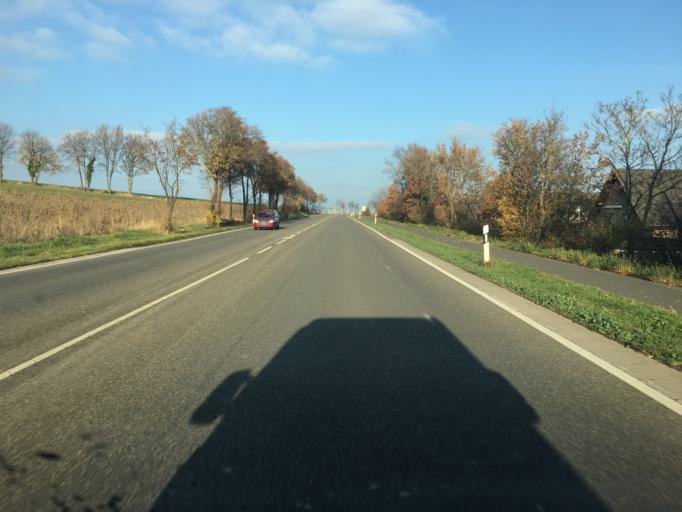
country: DE
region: North Rhine-Westphalia
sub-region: Regierungsbezirk Koln
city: Mechernich
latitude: 50.6112
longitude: 6.6425
